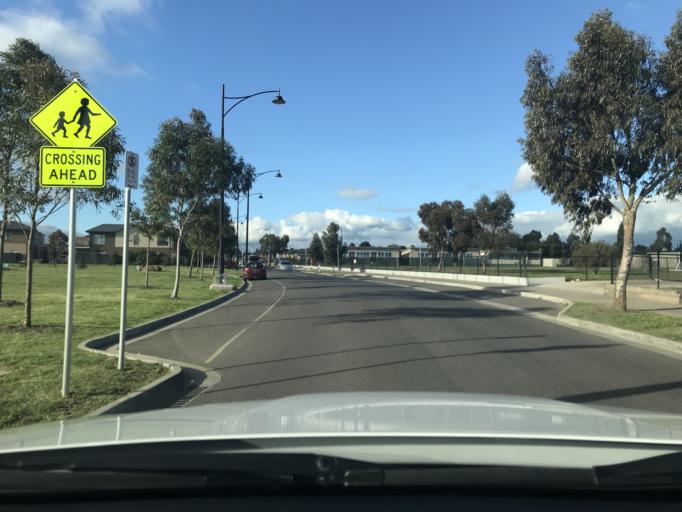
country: AU
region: Victoria
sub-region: Hume
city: Roxburgh Park
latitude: -37.5824
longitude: 144.9038
